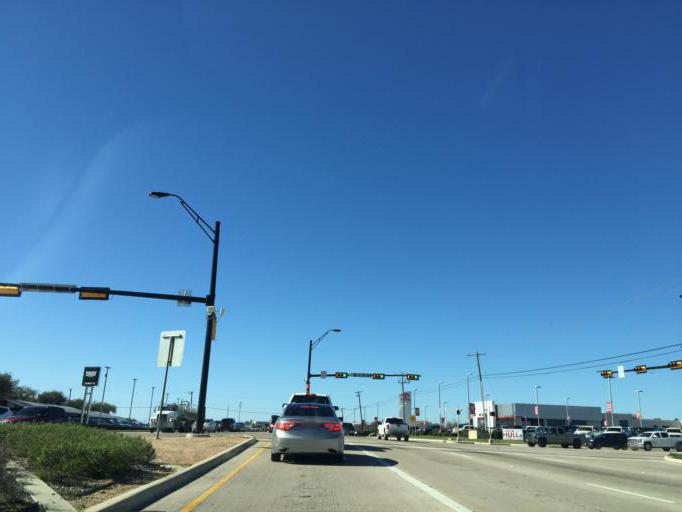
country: US
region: Texas
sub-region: Parker County
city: Hudson Oaks
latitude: 32.7566
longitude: -97.6984
